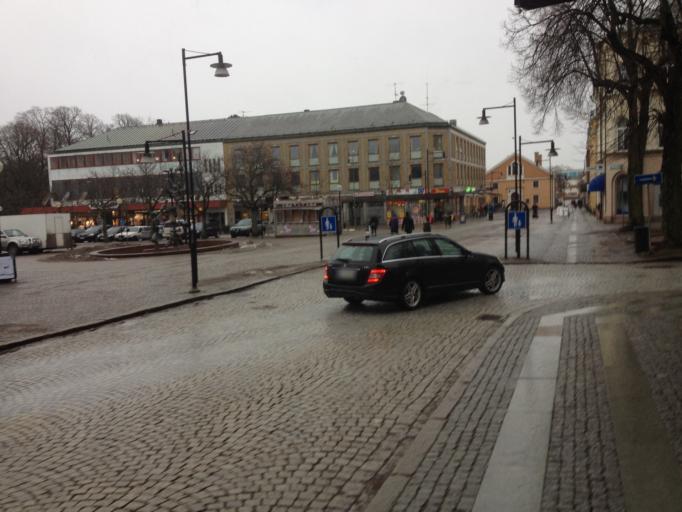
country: SE
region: Vaestra Goetaland
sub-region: Mariestads Kommun
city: Mariestad
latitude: 58.7097
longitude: 13.8227
